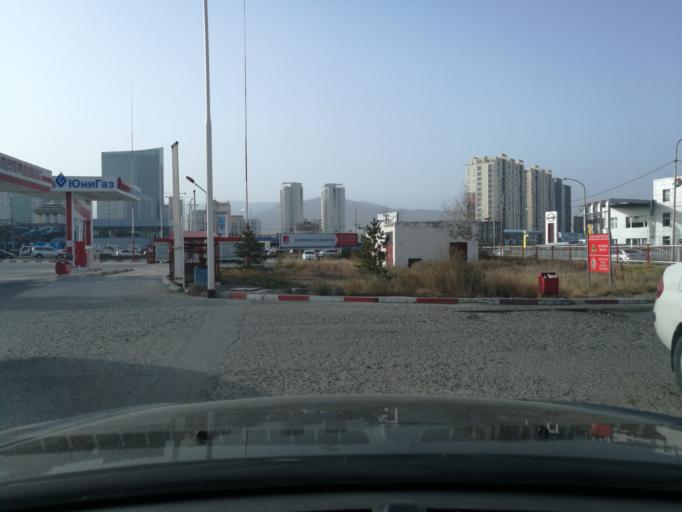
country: MN
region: Ulaanbaatar
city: Ulaanbaatar
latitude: 47.9090
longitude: 106.9126
